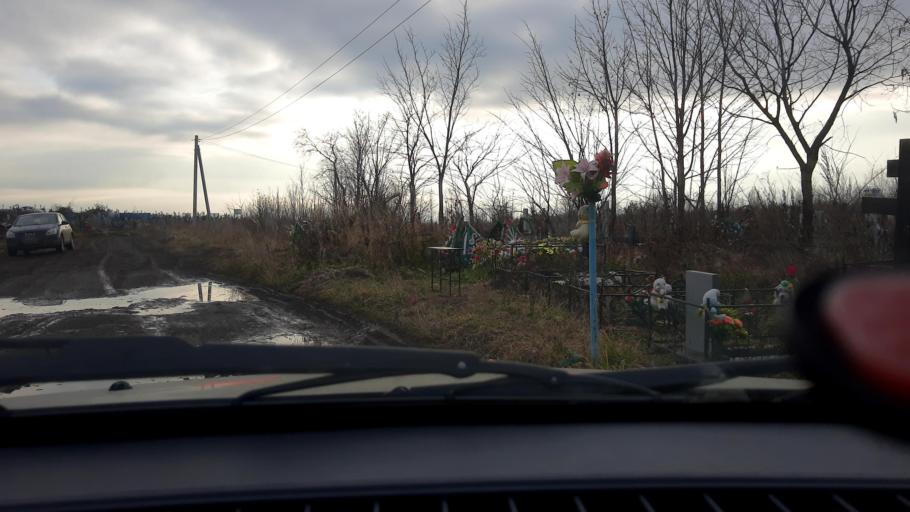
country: RU
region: Bashkortostan
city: Ufa
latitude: 54.8586
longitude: 56.1650
